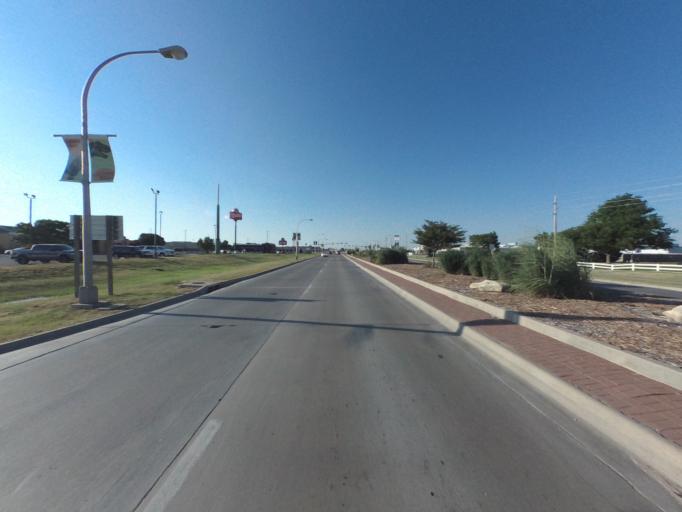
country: US
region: Kansas
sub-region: Ellis County
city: Hays
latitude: 38.9004
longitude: -99.3179
